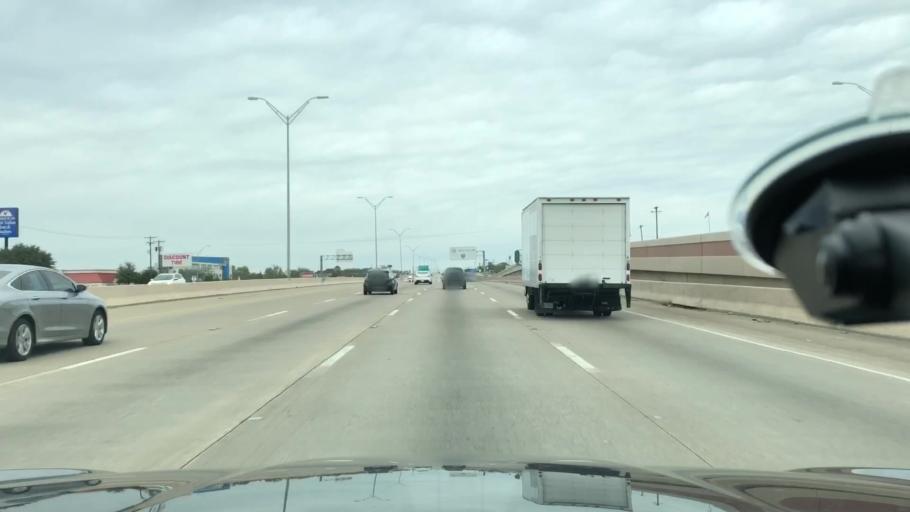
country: US
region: Texas
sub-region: Dallas County
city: DeSoto
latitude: 32.6085
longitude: -96.8229
